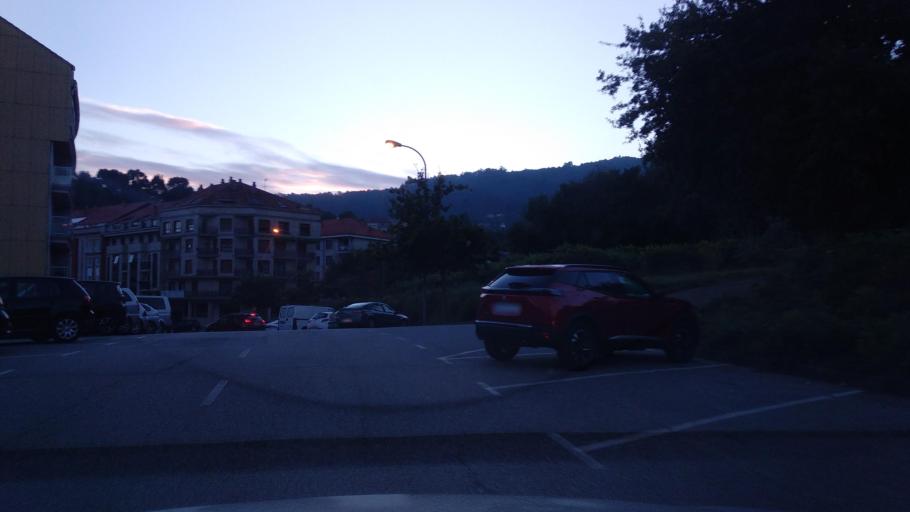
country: ES
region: Galicia
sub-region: Provincia de Pontevedra
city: Moana
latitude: 42.2899
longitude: -8.7336
